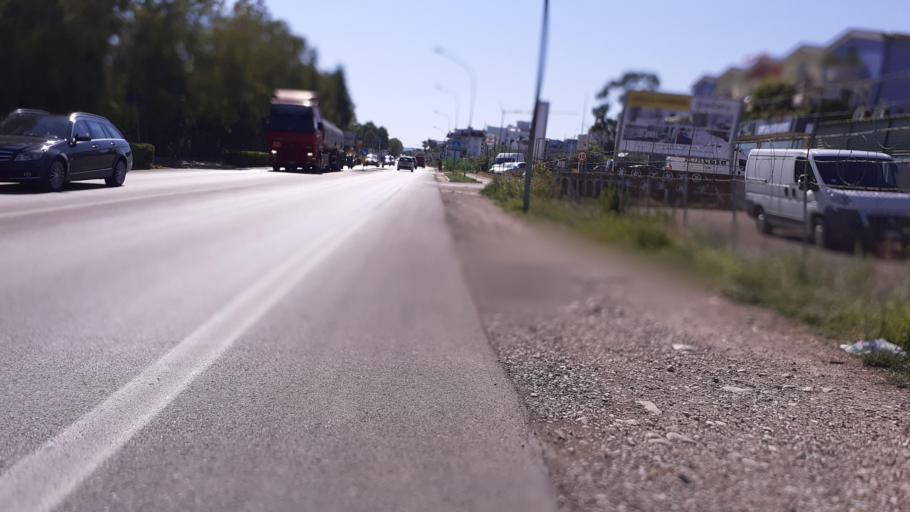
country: IT
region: Abruzzo
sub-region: Provincia di Chieti
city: Marina di Vasto
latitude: 42.0807
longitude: 14.7449
